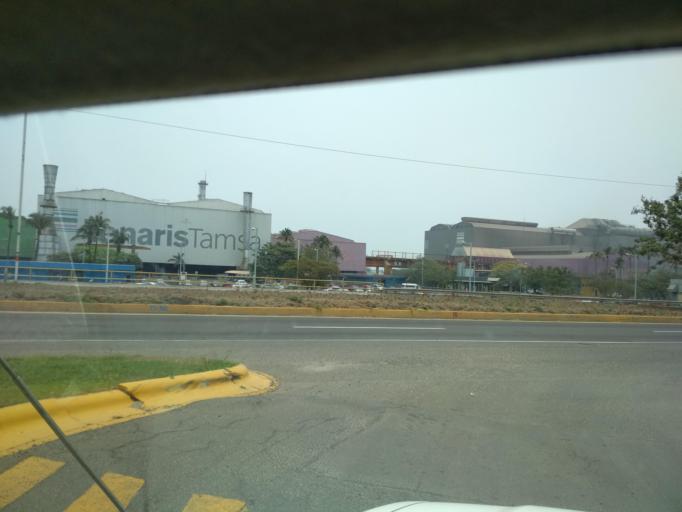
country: MX
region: Veracruz
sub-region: Veracruz
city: Oasis
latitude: 19.1771
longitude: -96.2446
